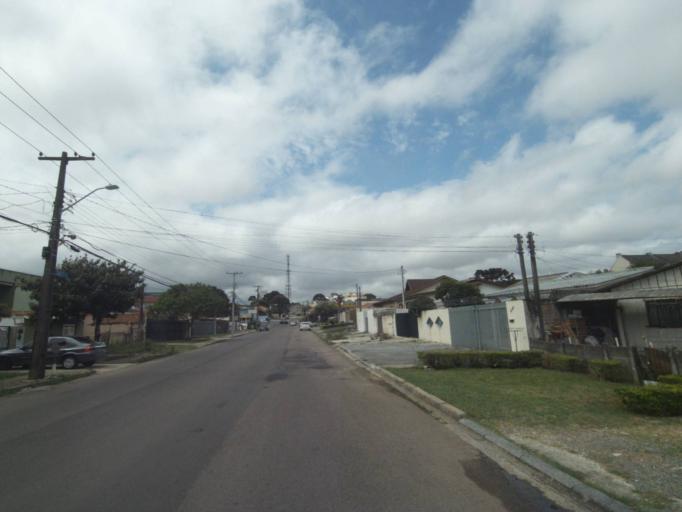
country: BR
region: Parana
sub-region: Pinhais
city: Pinhais
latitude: -25.4358
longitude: -49.2281
